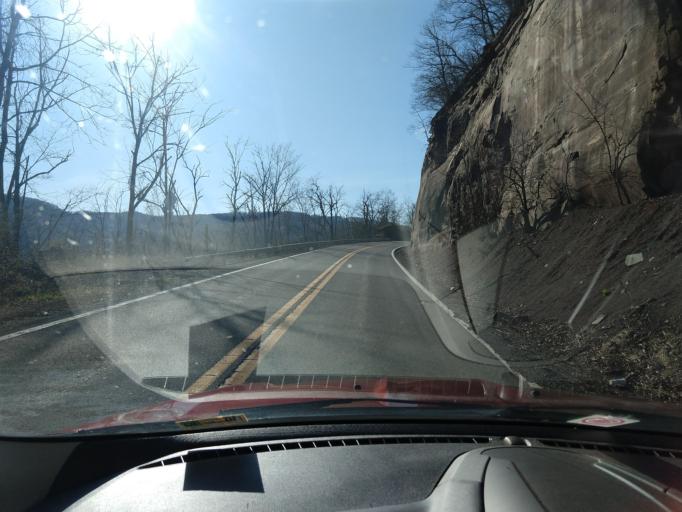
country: US
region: West Virginia
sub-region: Summers County
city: Hinton
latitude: 37.7367
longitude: -80.9077
